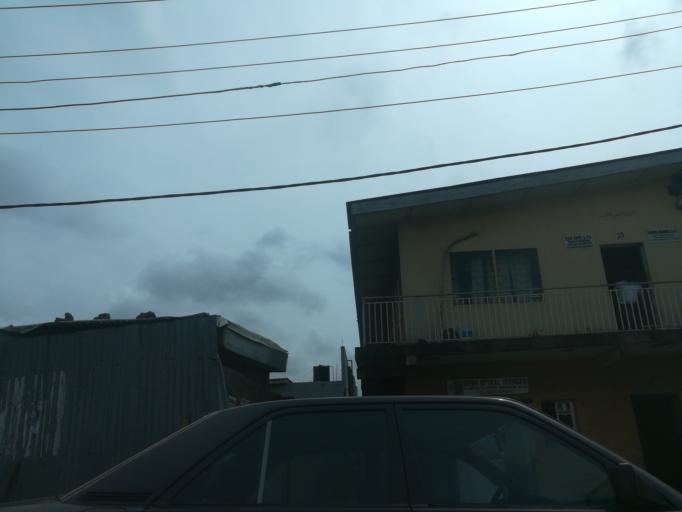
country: NG
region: Lagos
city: Ikeja
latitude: 6.6011
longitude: 3.3379
